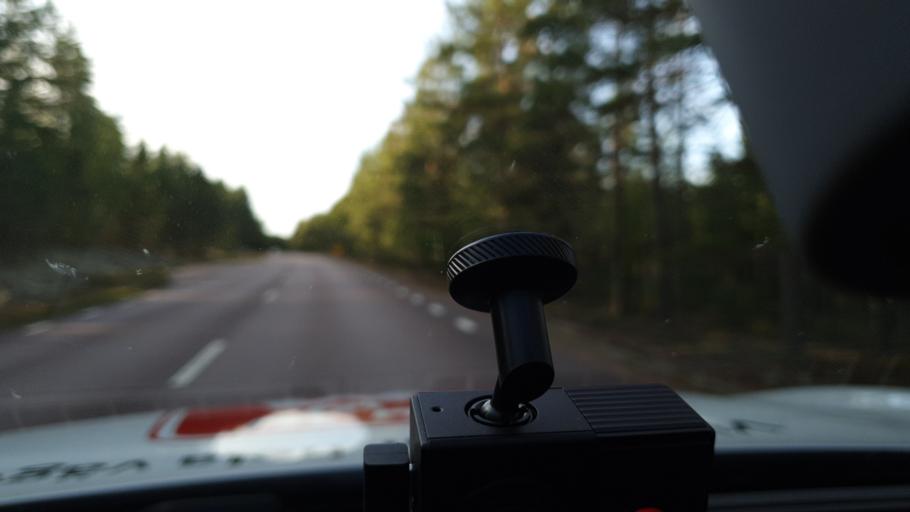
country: SE
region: Kalmar
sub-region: Kalmar Kommun
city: Trekanten
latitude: 56.8511
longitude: 16.1639
